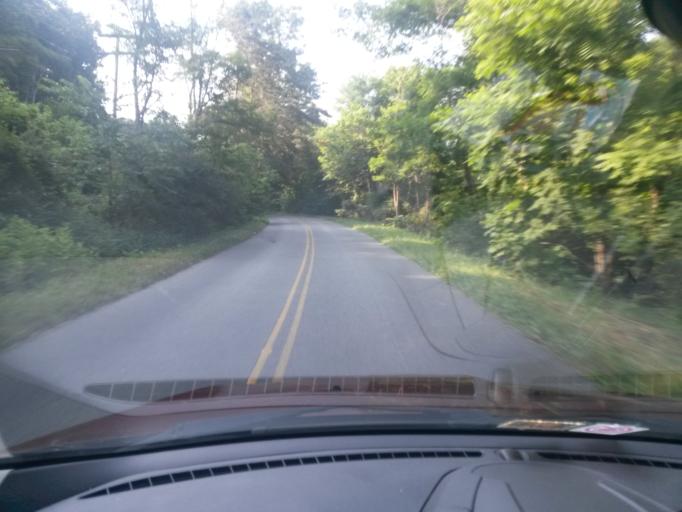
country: US
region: Virginia
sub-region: Giles County
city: Narrows
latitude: 37.3938
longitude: -80.7940
